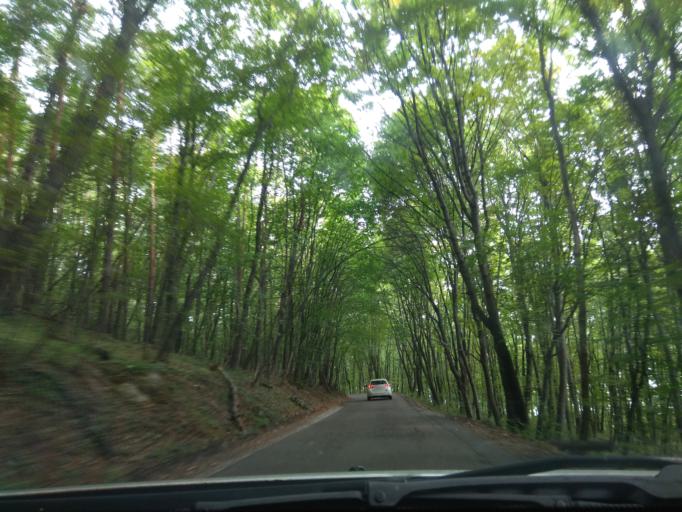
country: HU
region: Borsod-Abauj-Zemplen
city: Sajobabony
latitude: 48.0684
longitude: 20.6696
